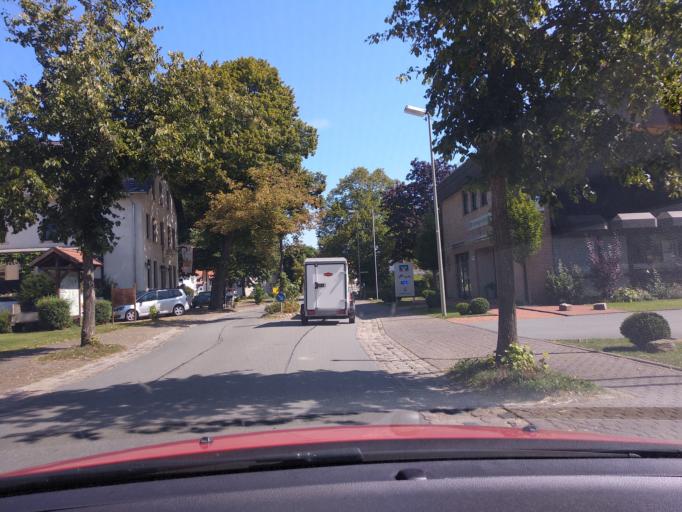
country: DE
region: North Rhine-Westphalia
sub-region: Regierungsbezirk Detmold
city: Willebadessen
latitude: 51.6550
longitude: 9.1199
